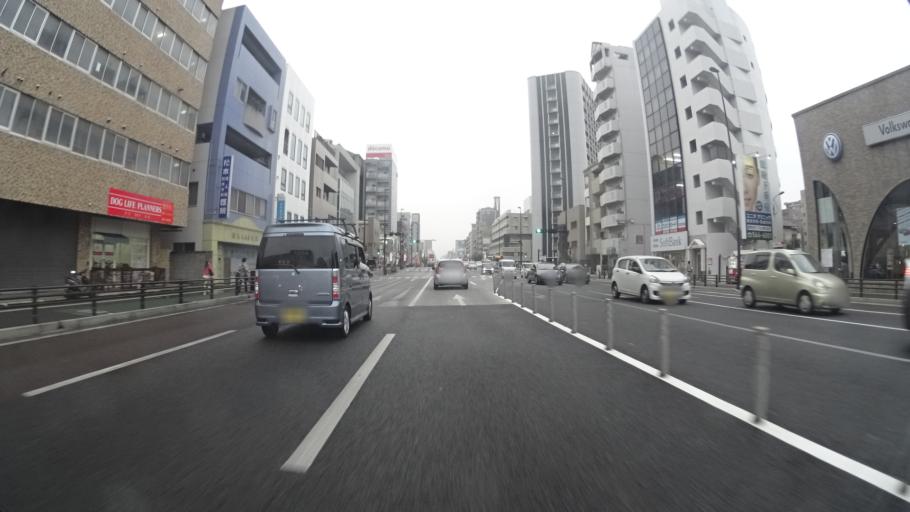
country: JP
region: Fukuoka
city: Fukuoka-shi
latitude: 33.5691
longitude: 130.4178
